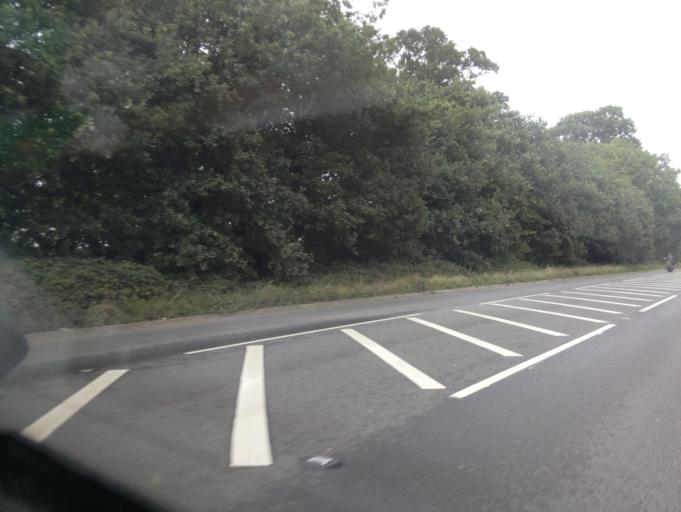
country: GB
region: England
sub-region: Devon
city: Uffculme
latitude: 50.8960
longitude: -3.3663
